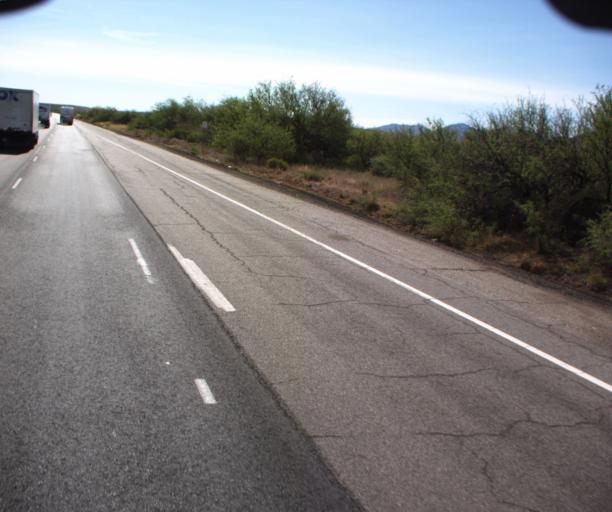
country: US
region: Arizona
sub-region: Cochise County
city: Mescal
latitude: 31.9752
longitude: -110.5075
